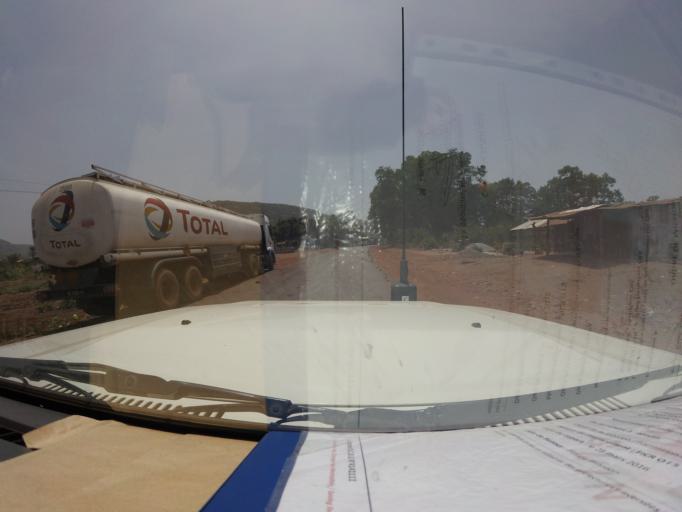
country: GN
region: Kindia
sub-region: Coyah
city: Coyah
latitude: 9.7862
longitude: -13.3130
